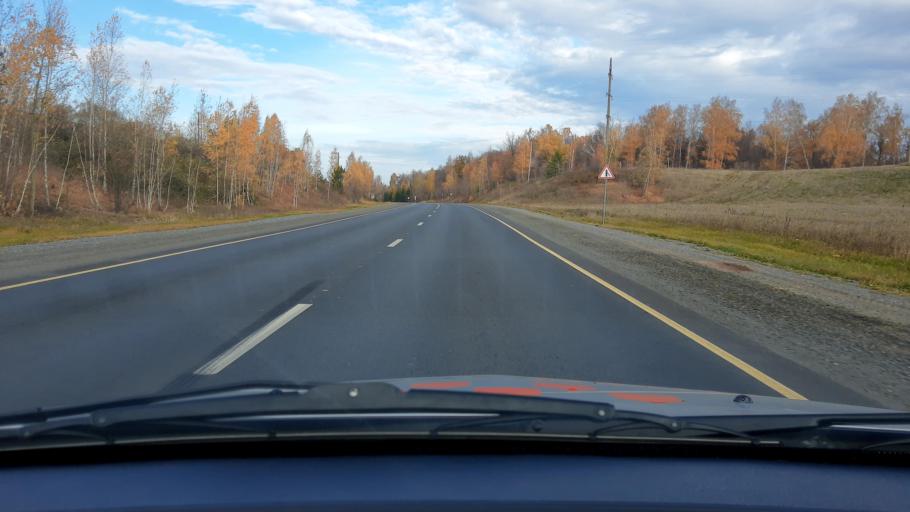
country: RU
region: Bashkortostan
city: Avdon
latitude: 54.8336
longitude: 55.7242
